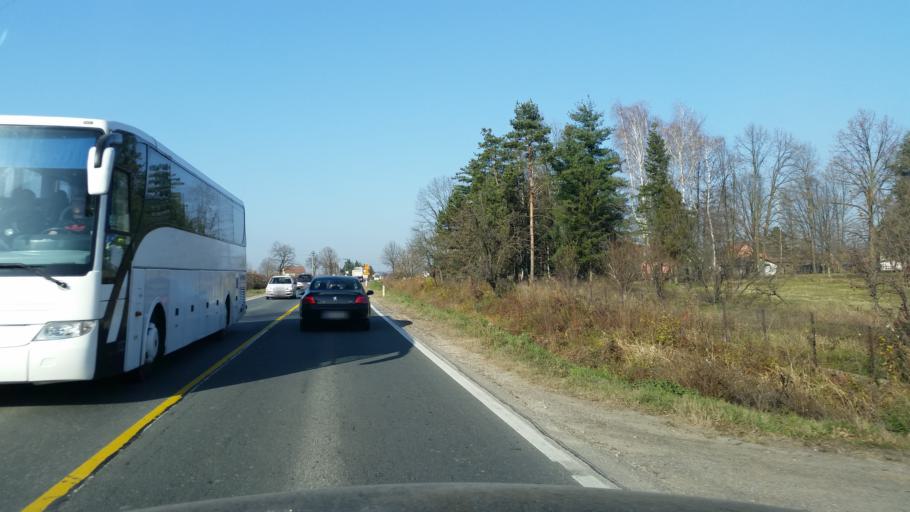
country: RS
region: Central Serbia
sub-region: Kolubarski Okrug
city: Ljig
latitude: 44.2970
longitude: 20.2612
